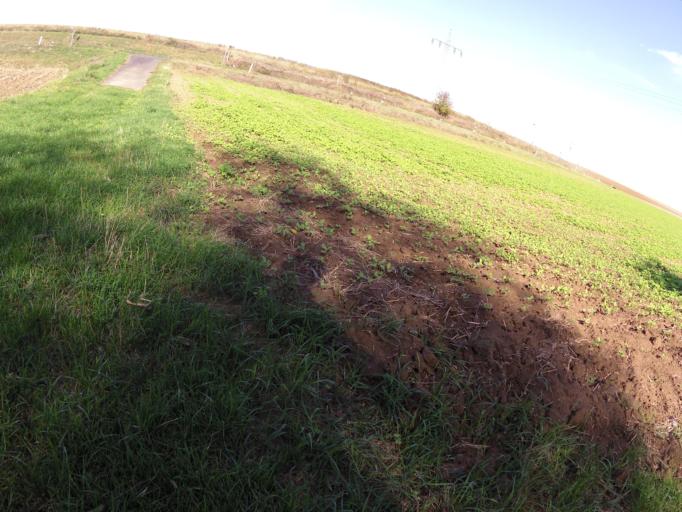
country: DE
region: Bavaria
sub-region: Regierungsbezirk Unterfranken
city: Biebelried
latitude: 49.7571
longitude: 10.0598
